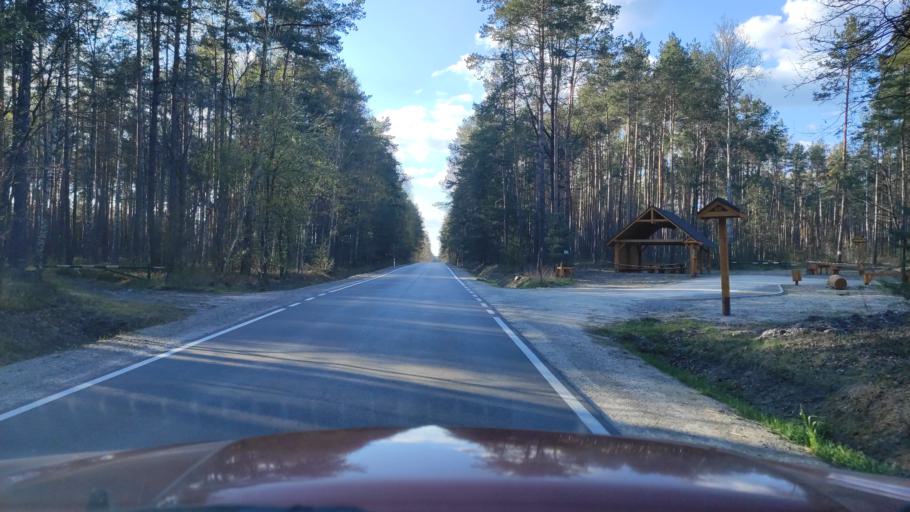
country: PL
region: Masovian Voivodeship
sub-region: Powiat zwolenski
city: Zwolen
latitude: 51.3895
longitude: 21.5505
